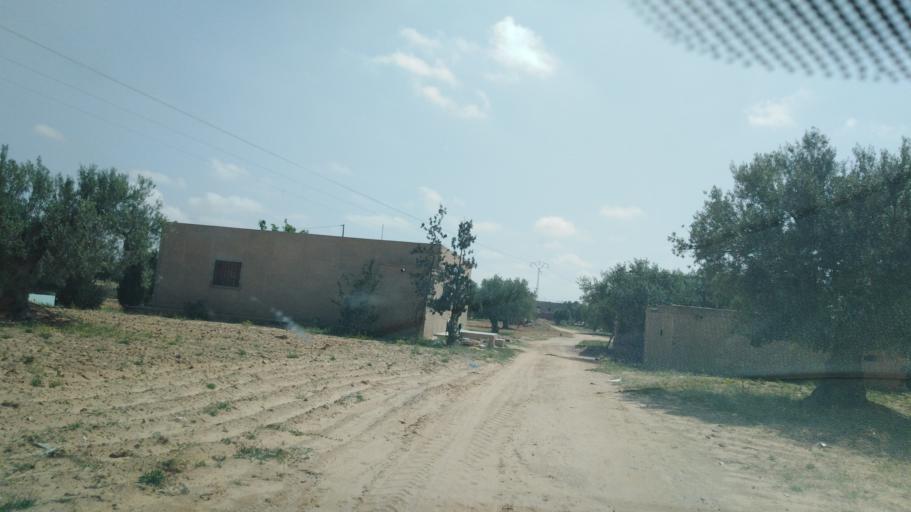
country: TN
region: Safaqis
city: Sfax
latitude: 34.7293
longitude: 10.5651
